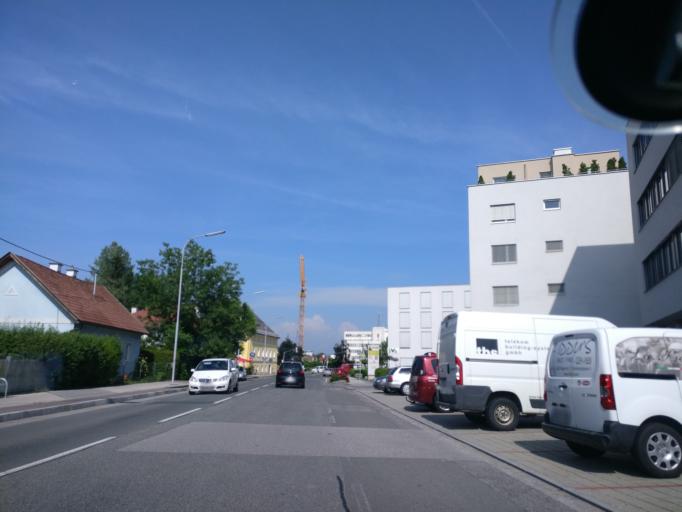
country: AT
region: Carinthia
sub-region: Klagenfurt am Woerthersee
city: Klagenfurt am Woerthersee
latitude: 46.6139
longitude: 14.2909
